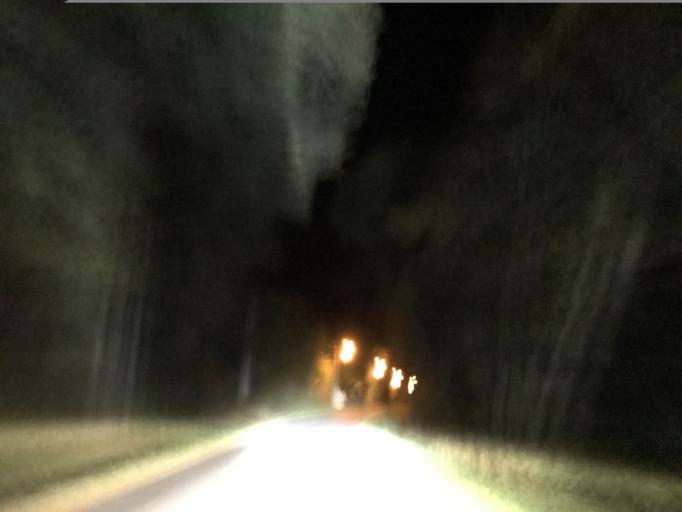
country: FR
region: Auvergne
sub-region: Departement du Puy-de-Dome
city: La Monnerie-le-Montel
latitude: 45.8691
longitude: 3.6104
